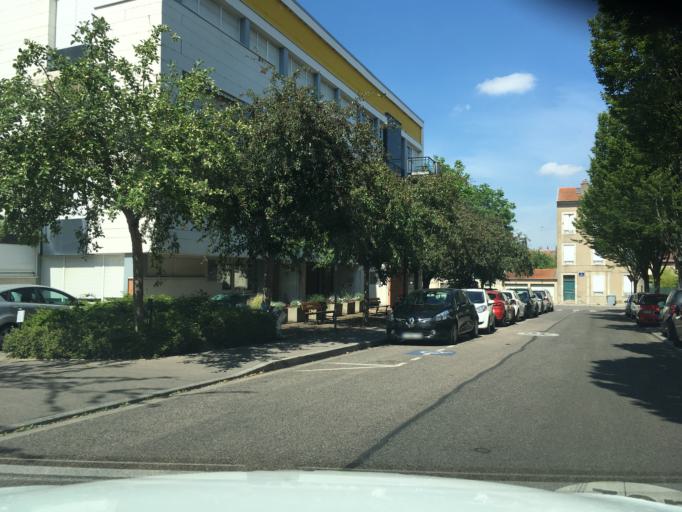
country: FR
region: Lorraine
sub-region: Departement de Meurthe-et-Moselle
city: Nancy
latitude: 48.6784
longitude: 6.1945
